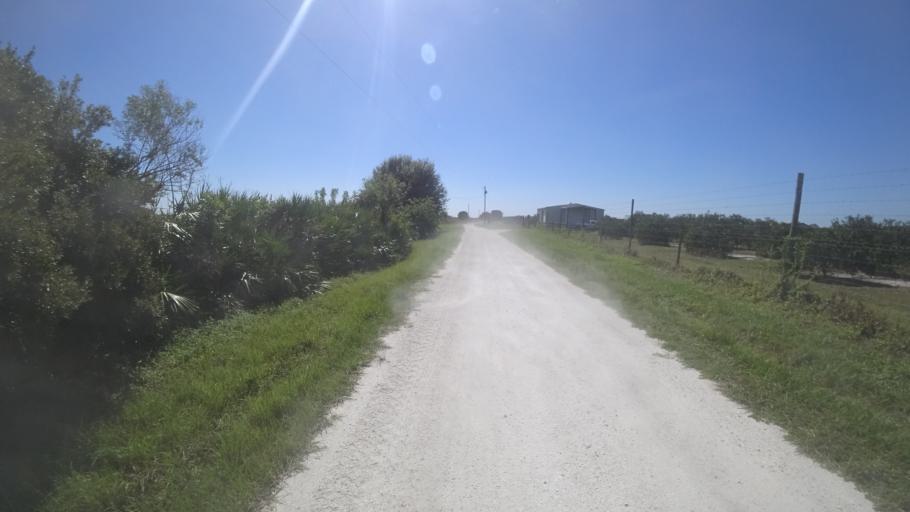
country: US
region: Florida
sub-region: Hillsborough County
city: Wimauma
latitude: 27.5345
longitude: -82.0877
